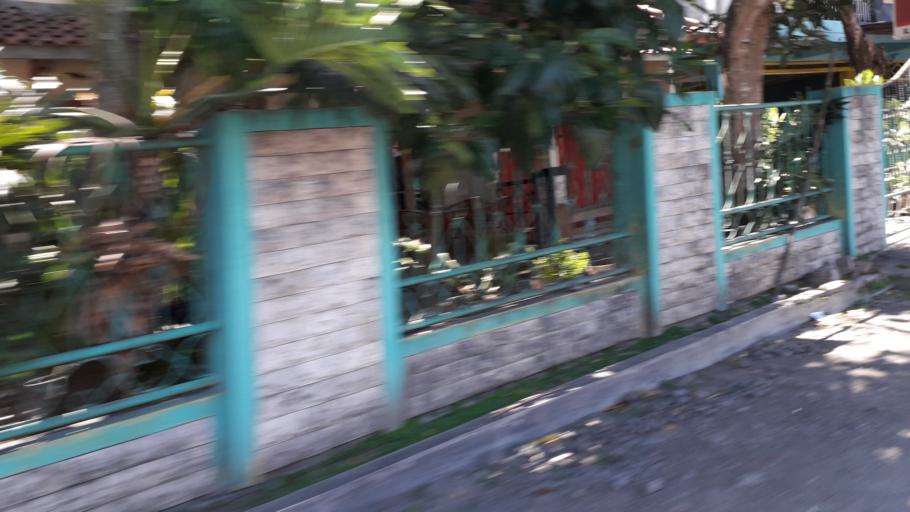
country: ID
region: Daerah Istimewa Yogyakarta
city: Pundong
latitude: -7.9675
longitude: 110.3198
